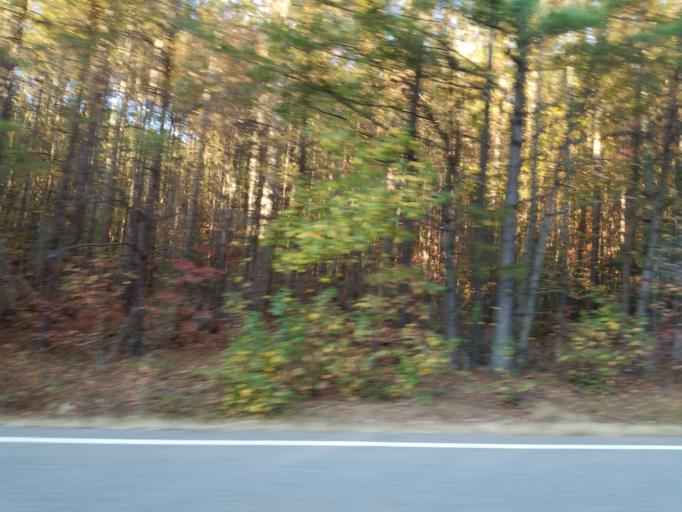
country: US
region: Georgia
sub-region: Dawson County
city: Dawsonville
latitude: 34.5380
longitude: -84.2108
